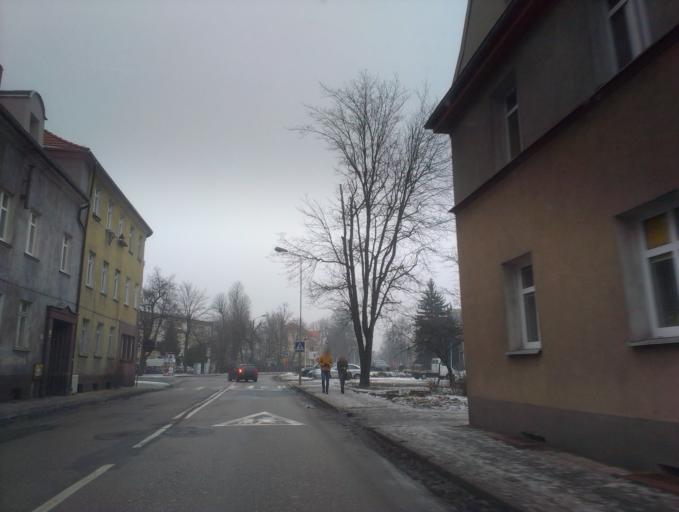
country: PL
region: Greater Poland Voivodeship
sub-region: Powiat pilski
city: Pila
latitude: 53.1549
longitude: 16.7374
